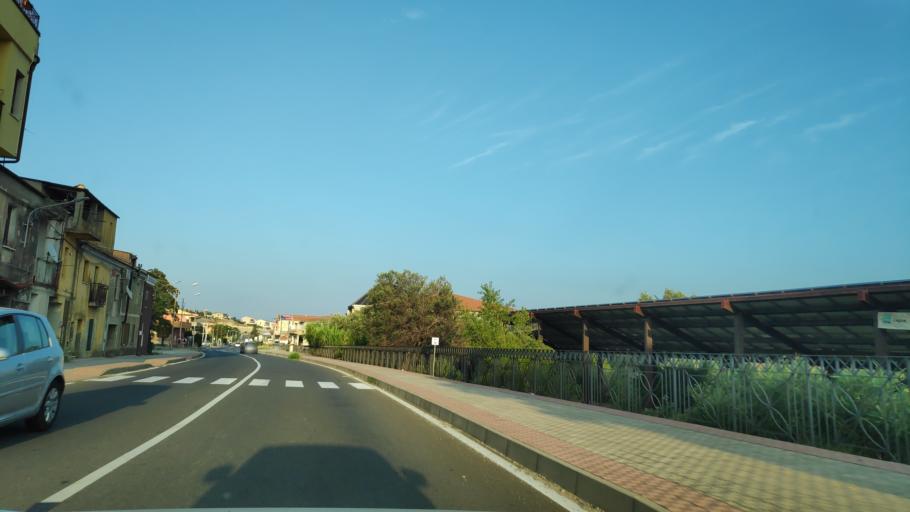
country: IT
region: Calabria
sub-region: Provincia di Catanzaro
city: Martelli-Laganosa
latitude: 38.6792
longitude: 16.5266
